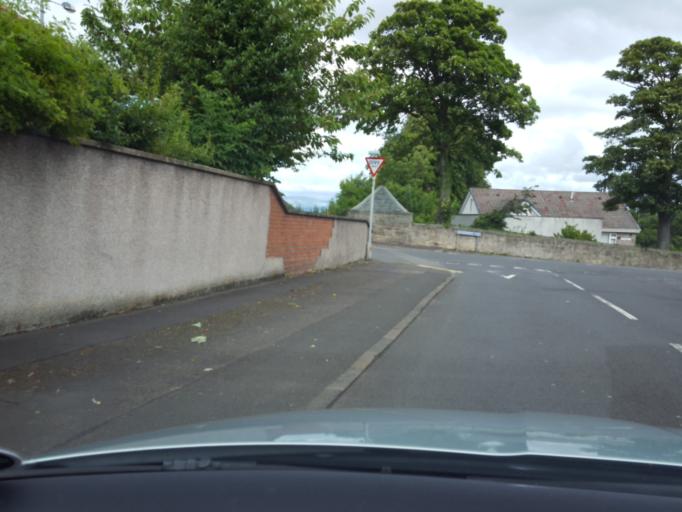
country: GB
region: Scotland
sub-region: Falkirk
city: Bo'ness
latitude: 56.0130
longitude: -3.5942
